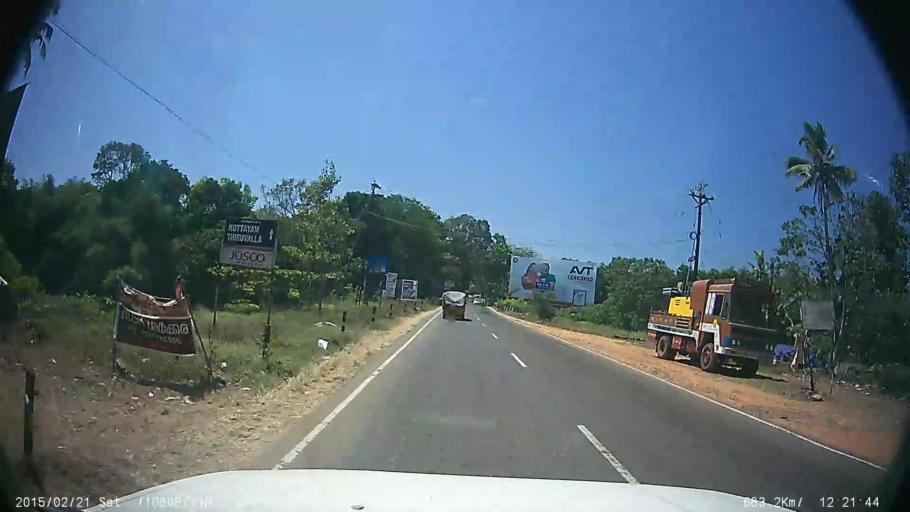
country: IN
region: Kerala
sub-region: Kottayam
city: Palackattumala
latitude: 9.6759
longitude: 76.5993
